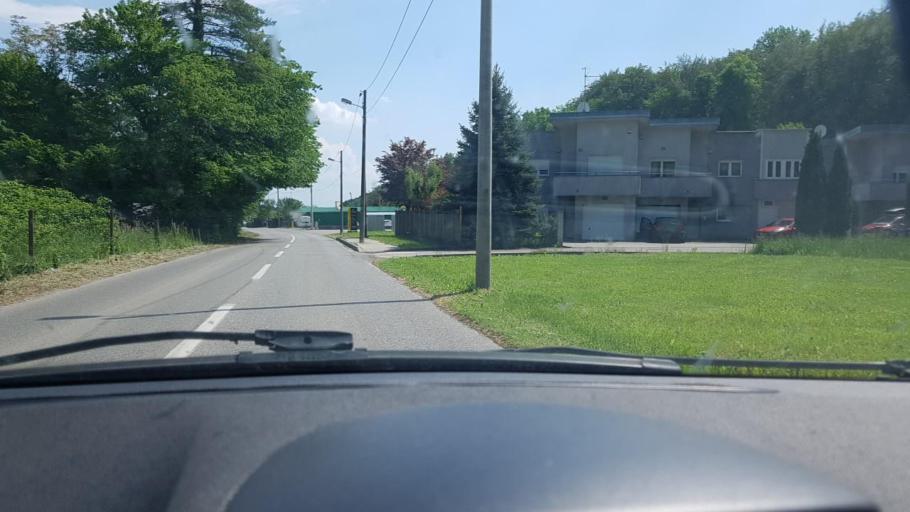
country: HR
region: Grad Zagreb
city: Dubrava
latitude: 45.8590
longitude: 16.0241
